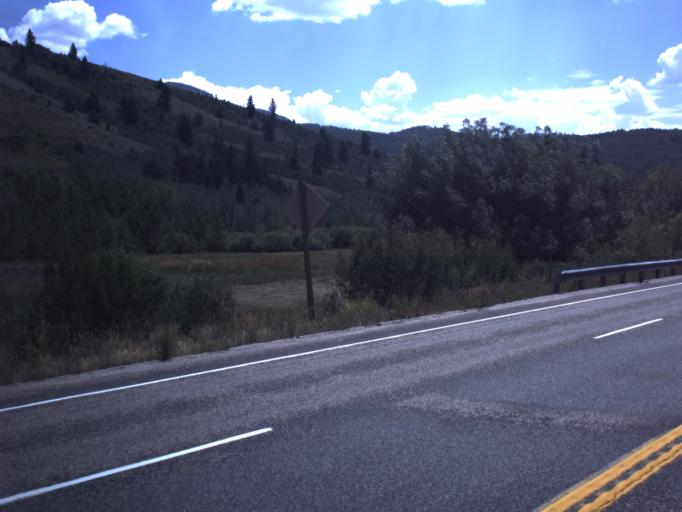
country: US
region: Utah
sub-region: Cache County
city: Richmond
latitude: 41.8780
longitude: -111.5643
